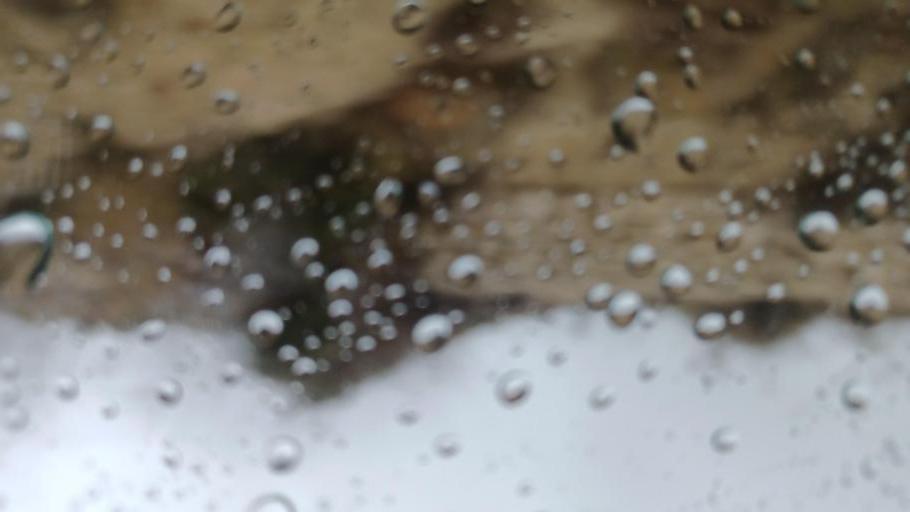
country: CY
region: Limassol
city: Pachna
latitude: 34.7836
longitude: 32.8237
